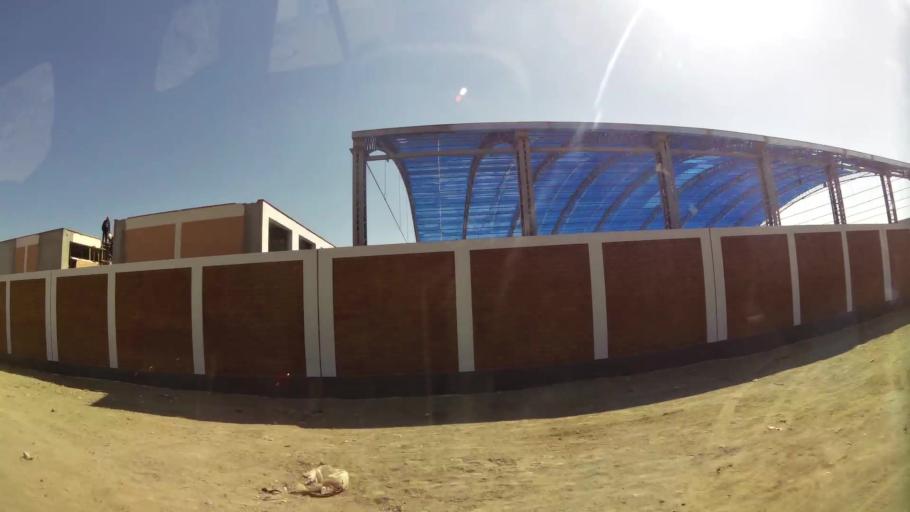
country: PE
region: Ica
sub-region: Provincia de Ica
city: La Tinguina
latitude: -14.0375
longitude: -75.7021
